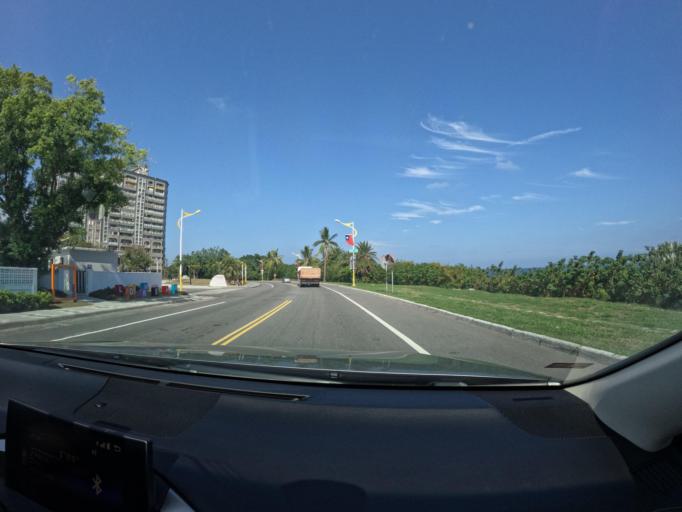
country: TW
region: Taiwan
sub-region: Hualien
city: Hualian
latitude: 23.9898
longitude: 121.6333
